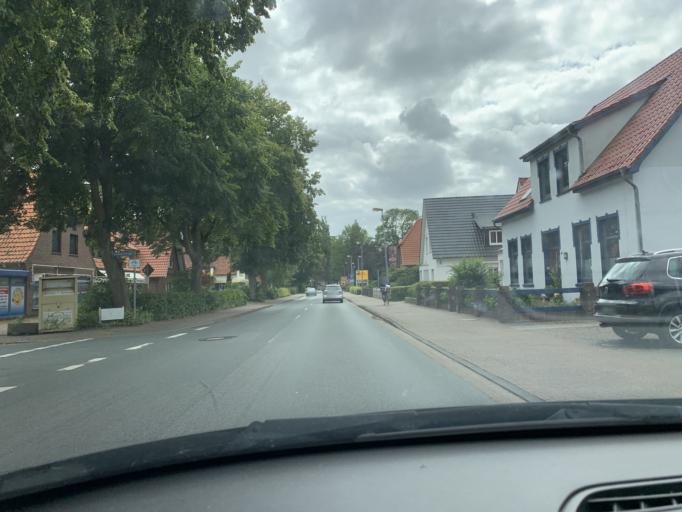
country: DE
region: Lower Saxony
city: Westerstede
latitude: 53.2635
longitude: 7.9336
